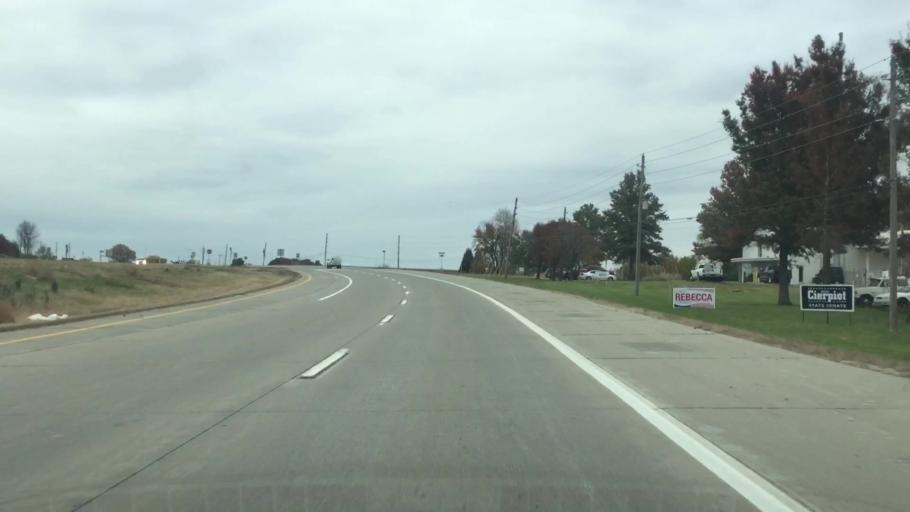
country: US
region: Missouri
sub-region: Jackson County
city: Lees Summit
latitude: 38.8911
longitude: -94.3731
